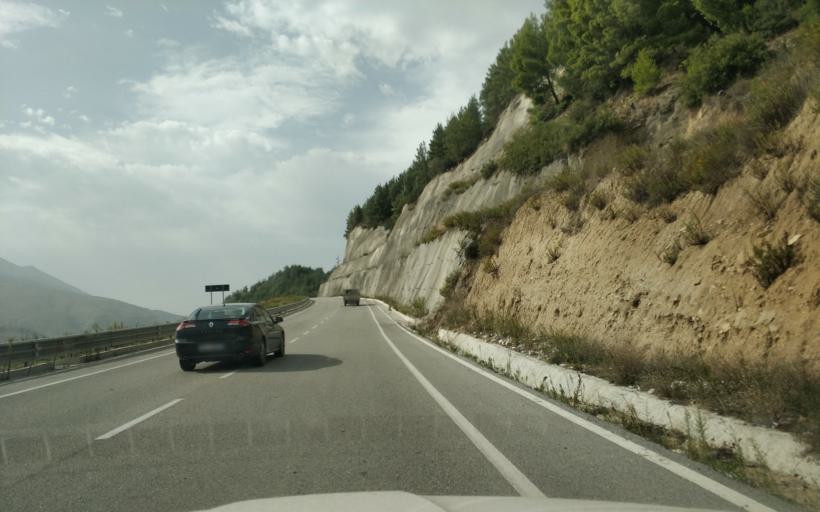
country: AL
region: Gjirokaster
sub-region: Rrethi i Tepelenes
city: Krahes
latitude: 40.3827
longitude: 19.8966
